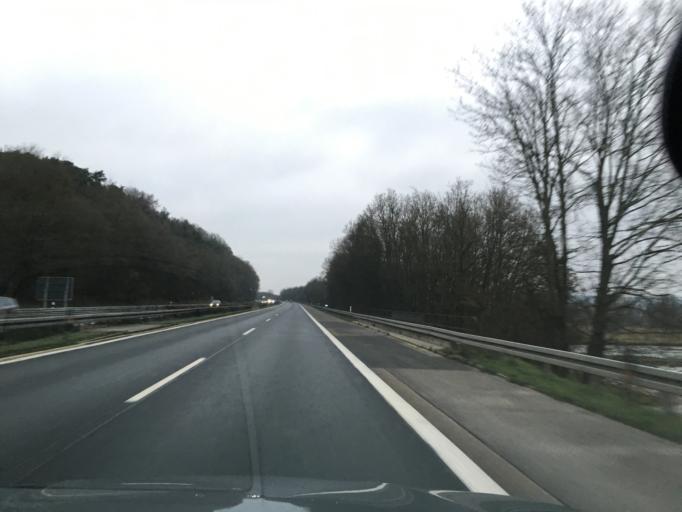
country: DE
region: Bavaria
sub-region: Upper Franconia
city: Schlusselfeld
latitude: 49.7539
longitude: 10.6122
